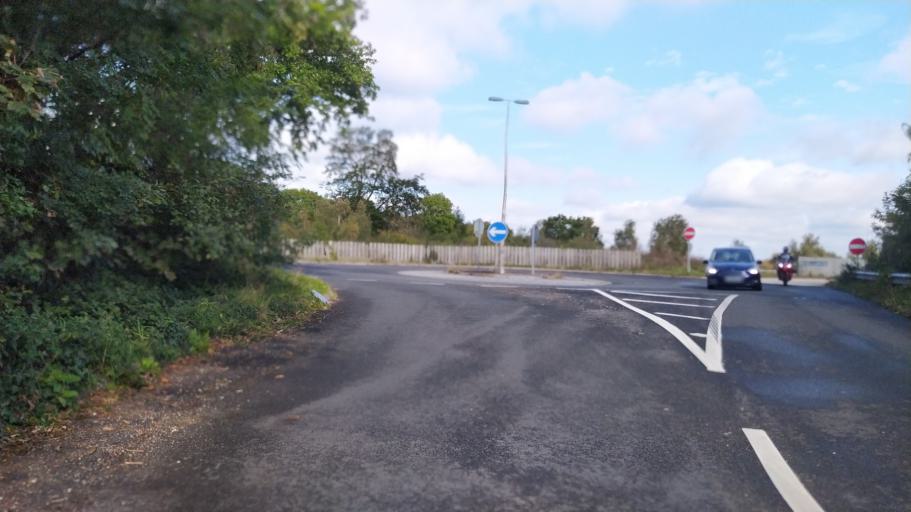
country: GB
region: England
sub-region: Hampshire
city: Ringwood
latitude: 50.8538
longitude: -1.7293
